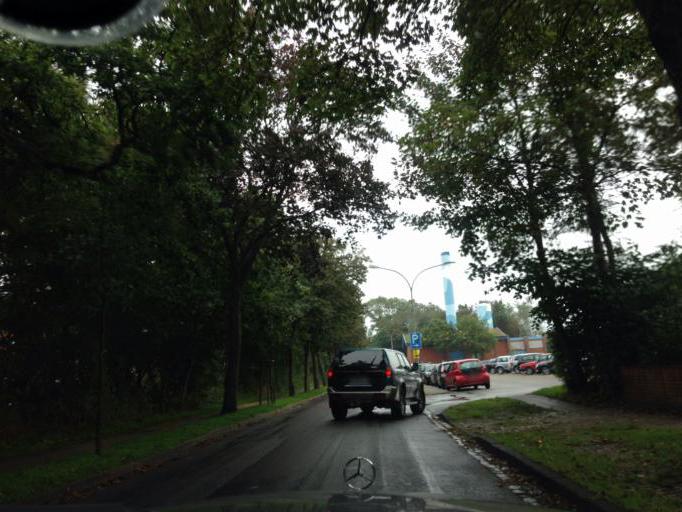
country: DE
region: Schleswig-Holstein
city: Wyk auf Fohr
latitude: 54.6842
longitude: 8.5659
